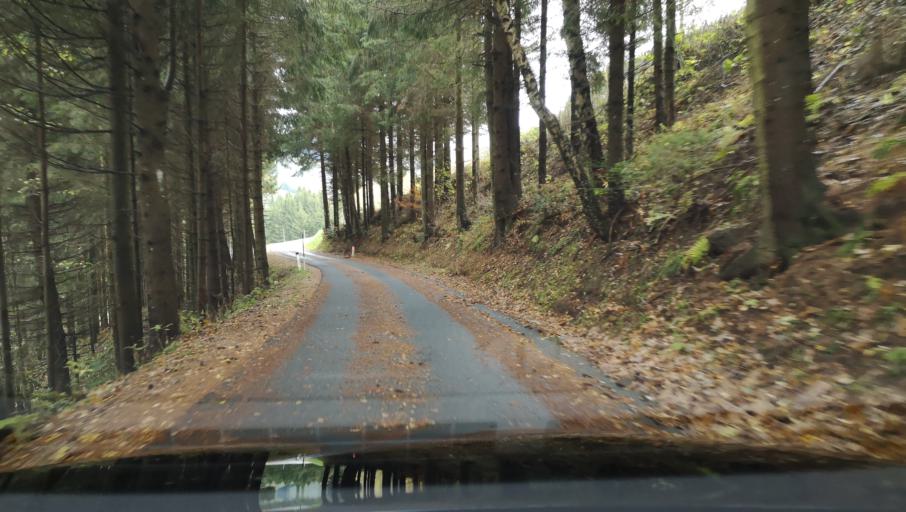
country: AT
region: Styria
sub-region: Politischer Bezirk Weiz
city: Gasen
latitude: 47.3564
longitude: 15.6010
